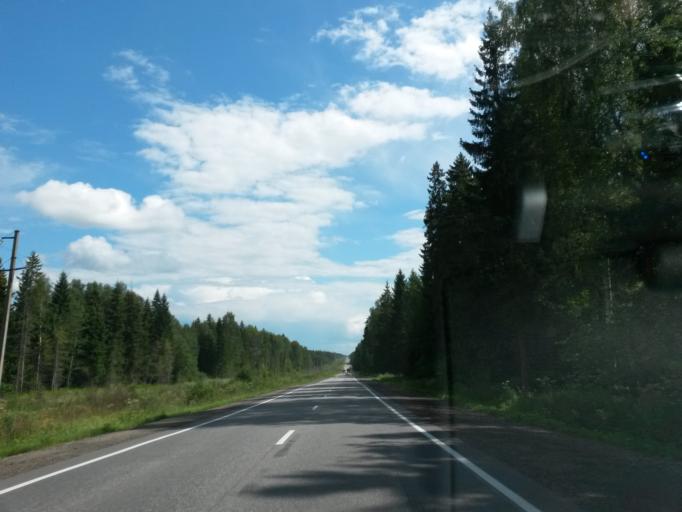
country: RU
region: Jaroslavl
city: Gavrilov-Yam
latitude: 57.2683
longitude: 39.9783
